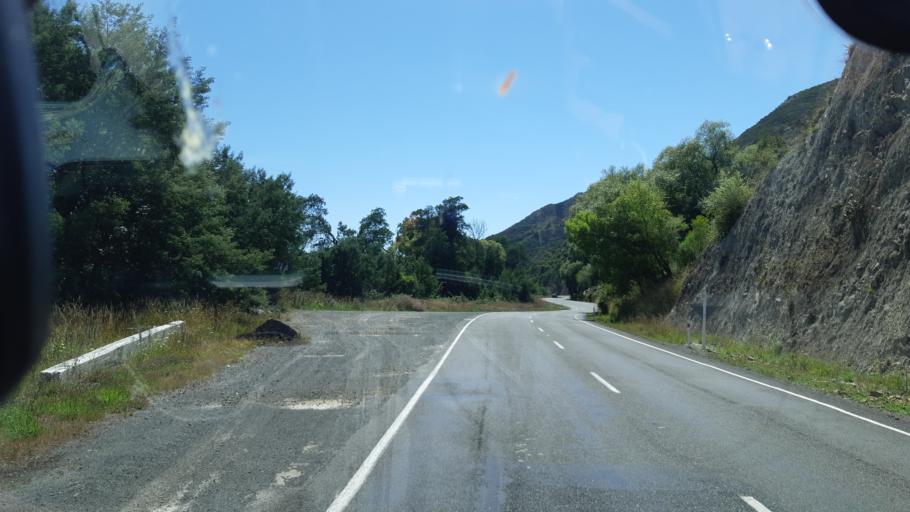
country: NZ
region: Canterbury
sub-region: Kaikoura District
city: Kaikoura
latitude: -42.6353
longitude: 173.3472
